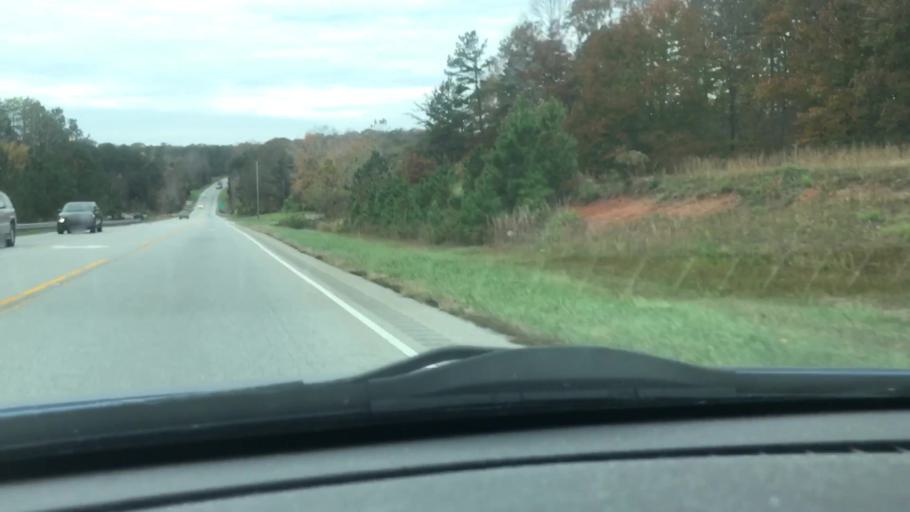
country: US
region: North Carolina
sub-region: Randolph County
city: Trinity
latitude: 35.7354
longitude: -79.9781
